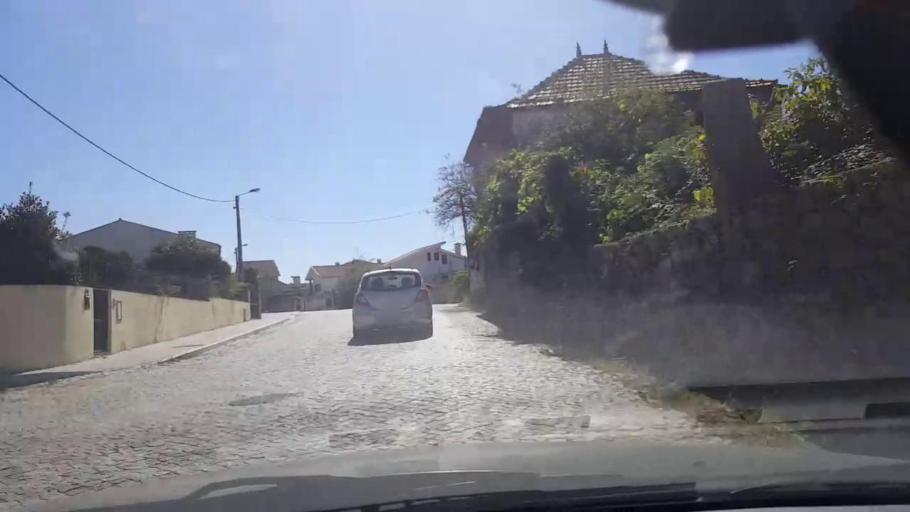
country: PT
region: Porto
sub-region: Vila do Conde
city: Arvore
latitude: 41.3169
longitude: -8.7224
